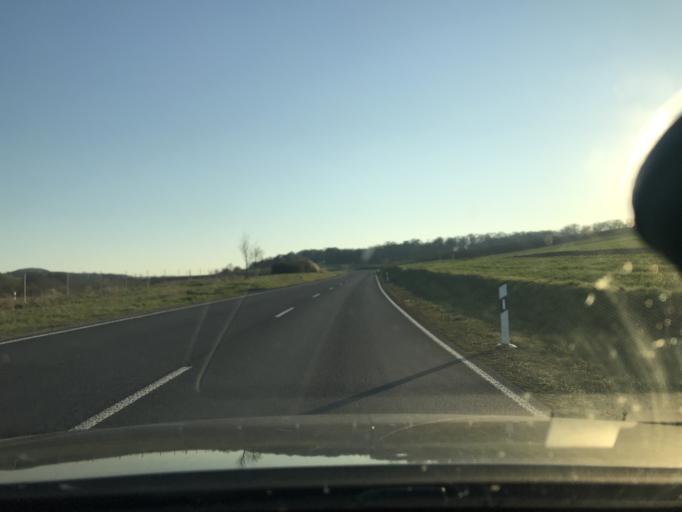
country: DE
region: Thuringia
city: Wipperdorf
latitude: 51.4428
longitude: 10.6531
